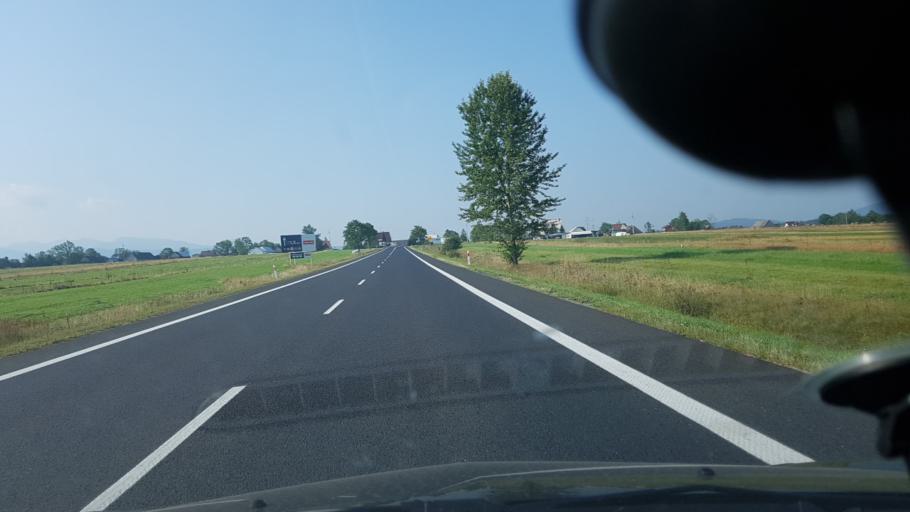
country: PL
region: Lesser Poland Voivodeship
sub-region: Powiat nowotarski
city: Chyzne
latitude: 49.4311
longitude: 19.6771
